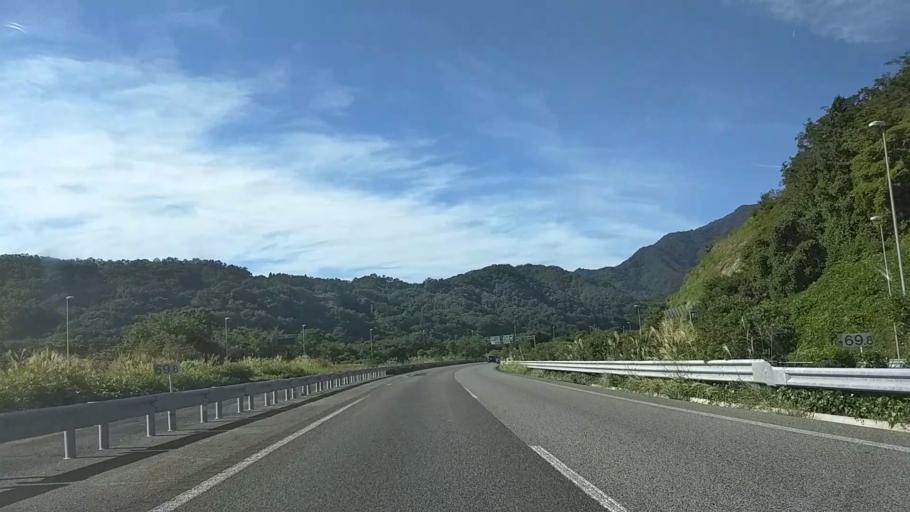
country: JP
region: Yamanashi
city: Otsuki
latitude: 35.6103
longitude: 138.9323
